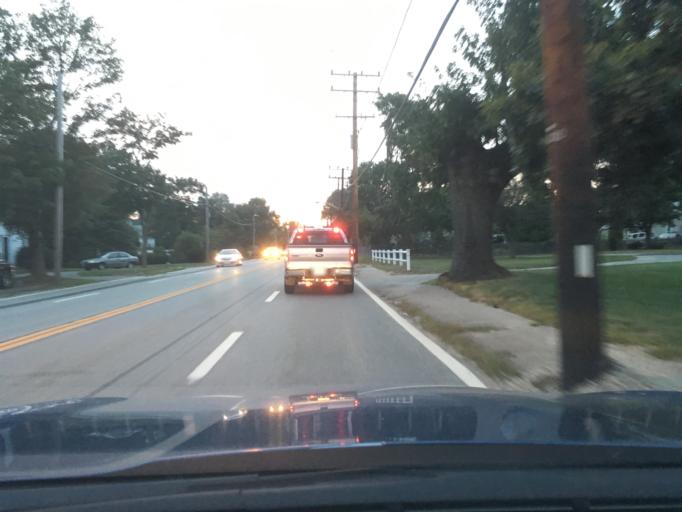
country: US
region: Rhode Island
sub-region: Kent County
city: Warwick
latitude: 41.7150
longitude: -71.4577
